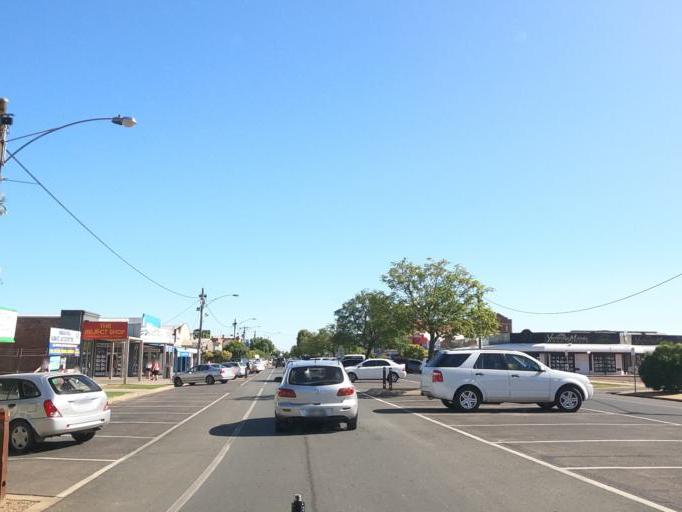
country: AU
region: Victoria
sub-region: Moira
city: Yarrawonga
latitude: -36.0148
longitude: 146.0045
